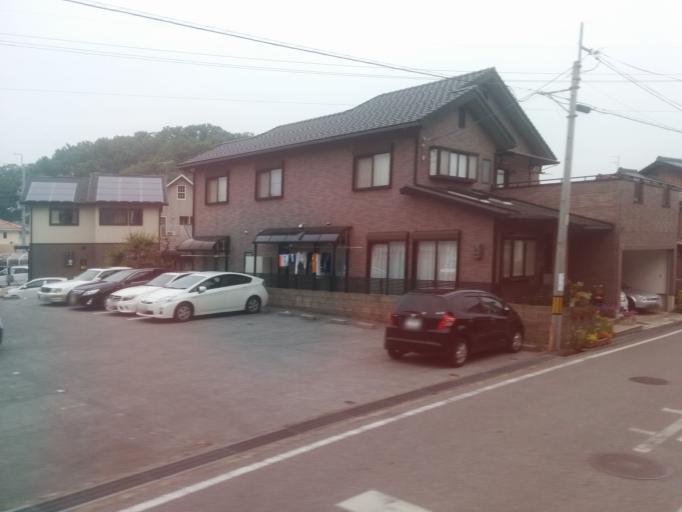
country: JP
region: Shiga Prefecture
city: Hikone
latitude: 35.2553
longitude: 136.2581
